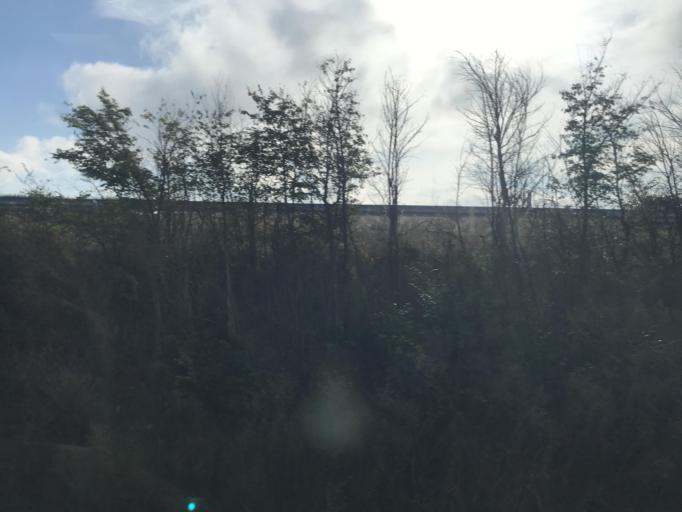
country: ES
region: Castille and Leon
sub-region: Provincia de Burgos
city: Briviesca
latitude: 42.5652
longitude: -3.3089
